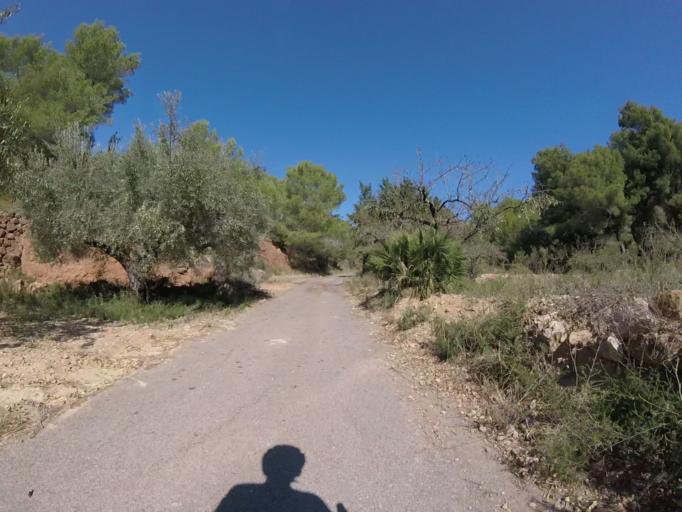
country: ES
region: Valencia
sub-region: Provincia de Castello
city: Cabanes
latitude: 40.1412
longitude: 0.1024
